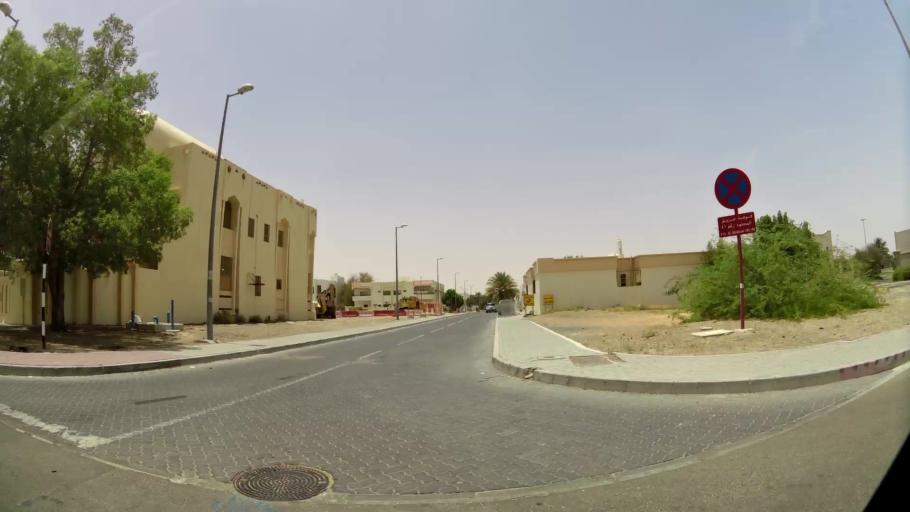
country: AE
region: Abu Dhabi
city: Al Ain
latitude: 24.2152
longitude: 55.7232
